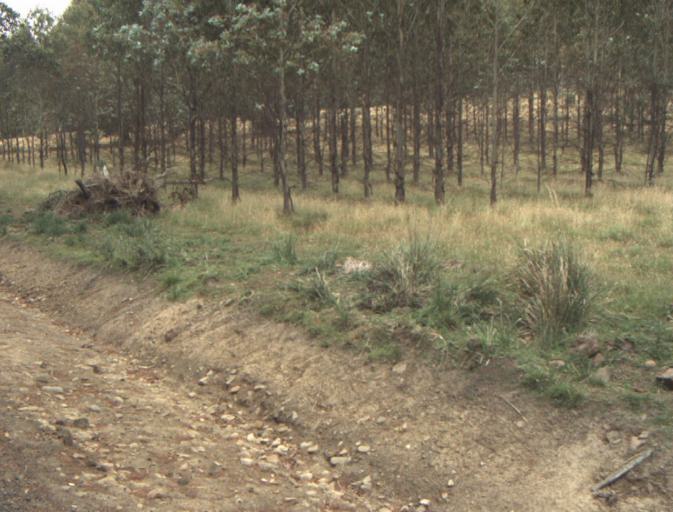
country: AU
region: Tasmania
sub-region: Northern Midlands
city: Evandale
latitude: -41.4555
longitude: 147.4448
